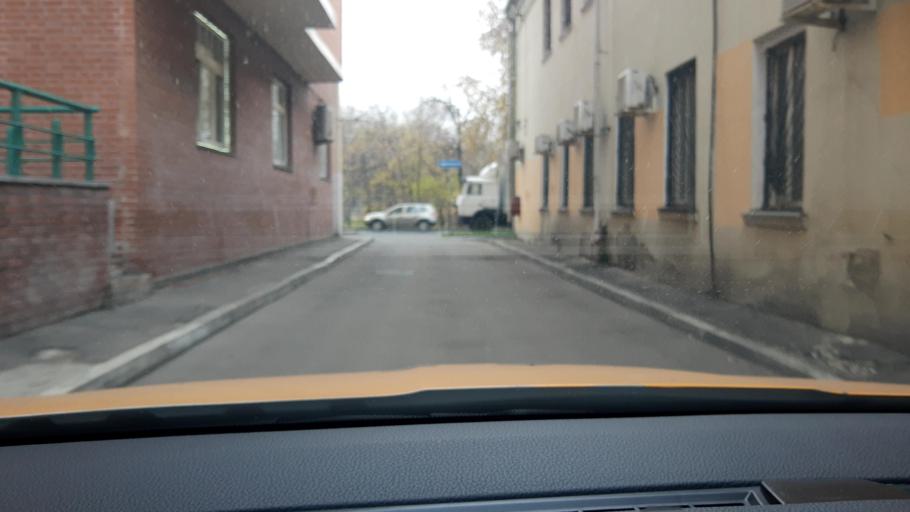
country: RU
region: Moscow
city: Tekstil'shchiki
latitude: 55.6938
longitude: 37.7424
